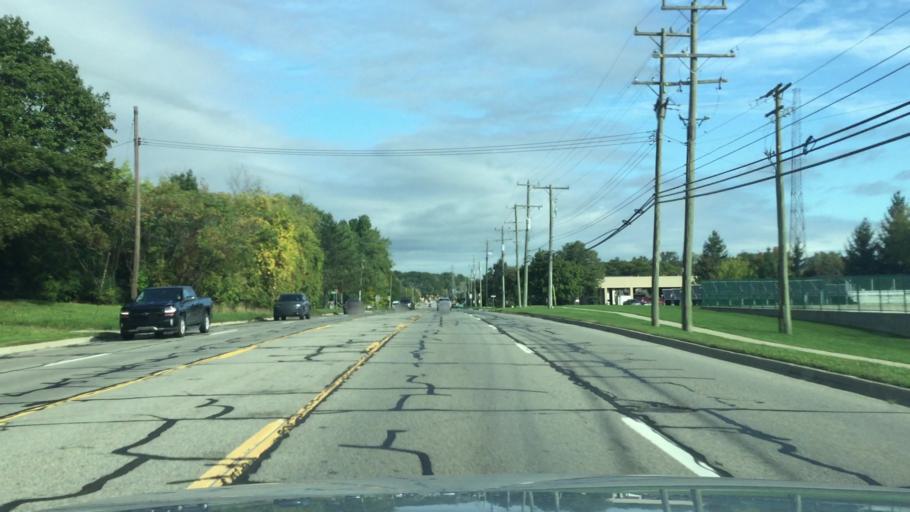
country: US
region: Michigan
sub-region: Oakland County
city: Orchard Lake
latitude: 42.5683
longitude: -83.3619
